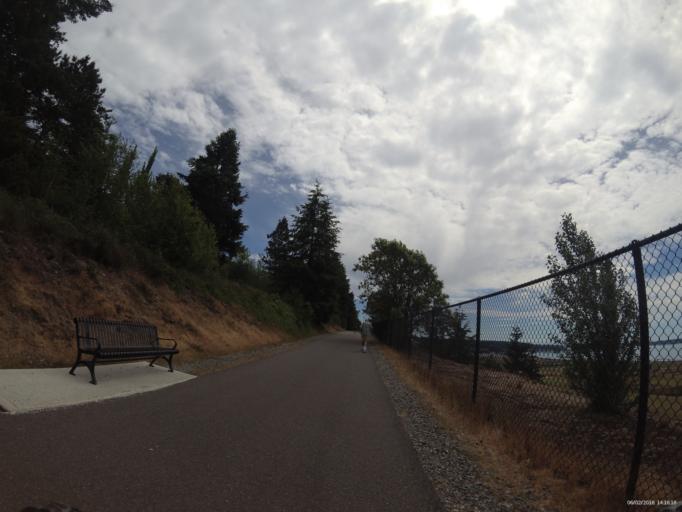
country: US
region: Washington
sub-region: Pierce County
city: University Place
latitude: 47.2067
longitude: -122.5693
